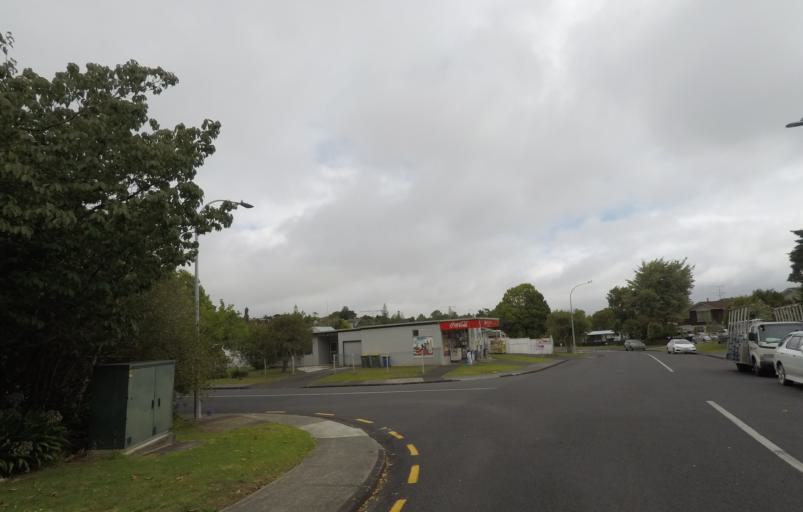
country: NZ
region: Auckland
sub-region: Auckland
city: Titirangi
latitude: -36.9357
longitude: 174.6697
